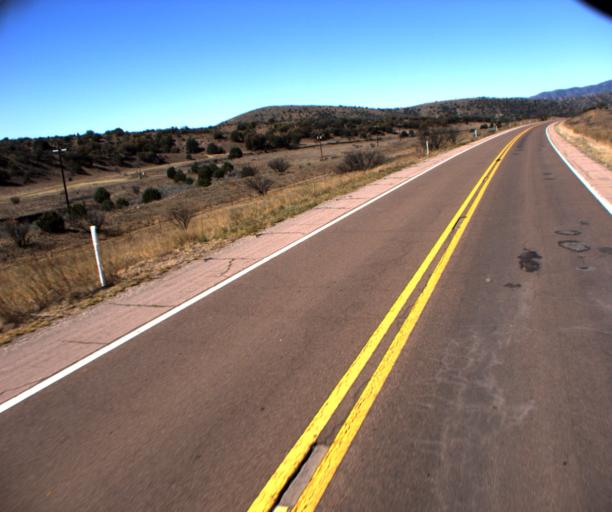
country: US
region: Arizona
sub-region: Pima County
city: Corona de Tucson
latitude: 31.6633
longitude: -110.6830
